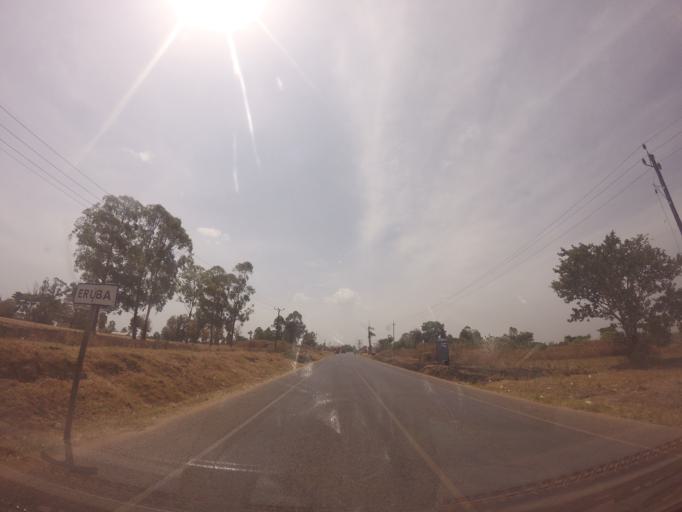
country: UG
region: Northern Region
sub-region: Arua District
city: Arua
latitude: 2.9608
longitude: 30.9169
